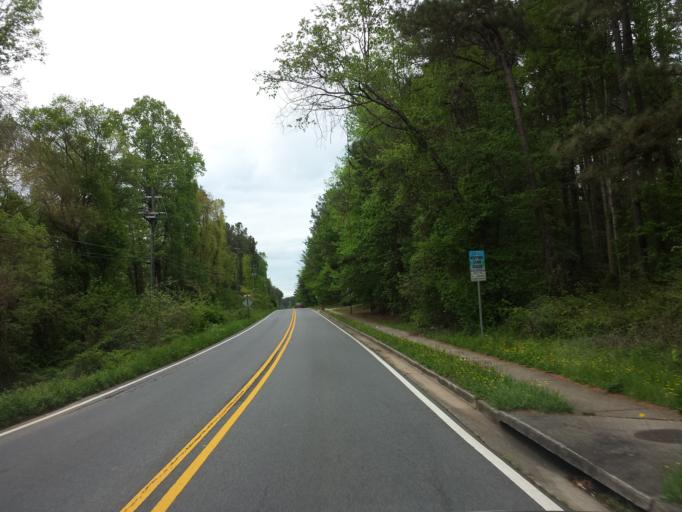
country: US
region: Georgia
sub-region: Cherokee County
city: Woodstock
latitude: 34.0500
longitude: -84.4848
